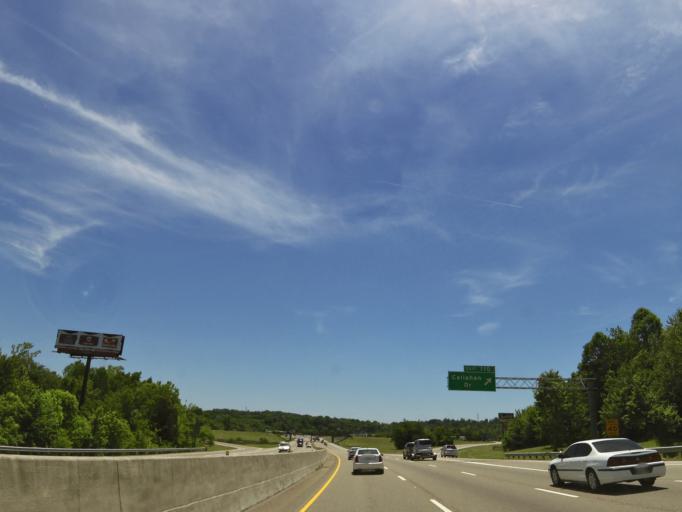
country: US
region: Tennessee
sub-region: Knox County
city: Knoxville
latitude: 36.0287
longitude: -83.9988
